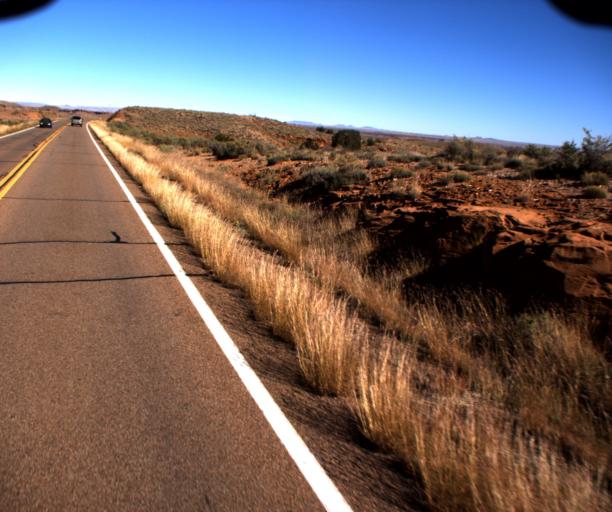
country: US
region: Arizona
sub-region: Navajo County
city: Holbrook
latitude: 34.8432
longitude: -110.1467
